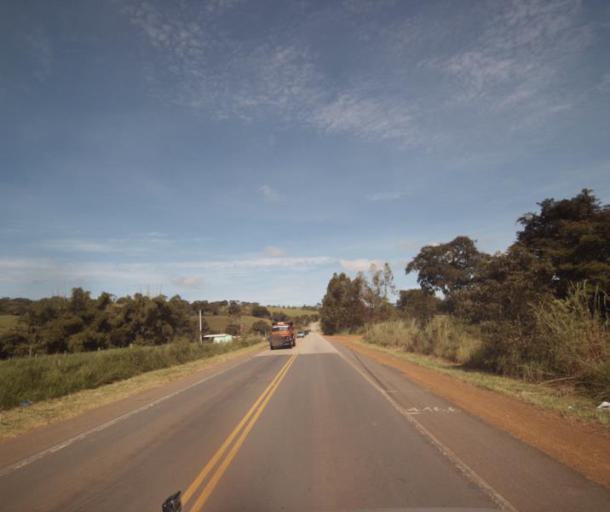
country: BR
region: Goias
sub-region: Abadiania
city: Abadiania
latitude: -16.1079
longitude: -48.8742
